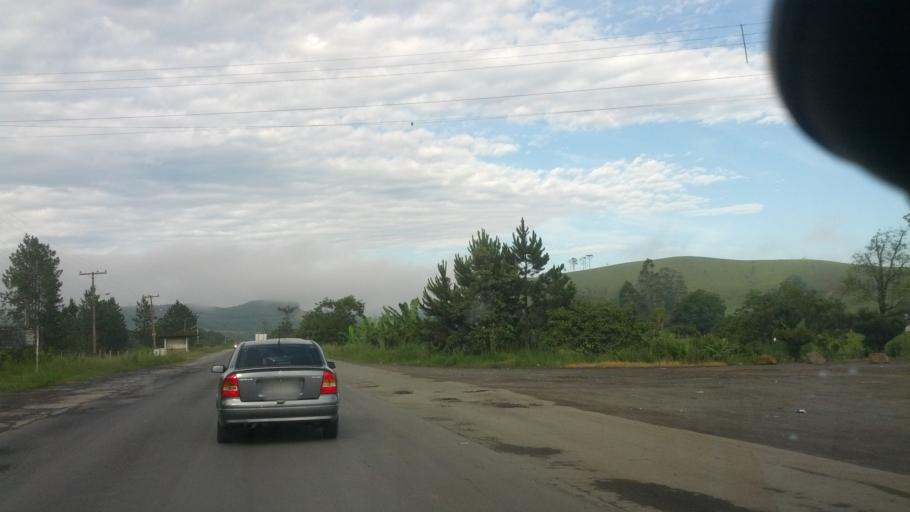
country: BR
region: Santa Catarina
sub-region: Otacilio Costa
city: Otacilio Costa
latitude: -27.2502
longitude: -49.9901
